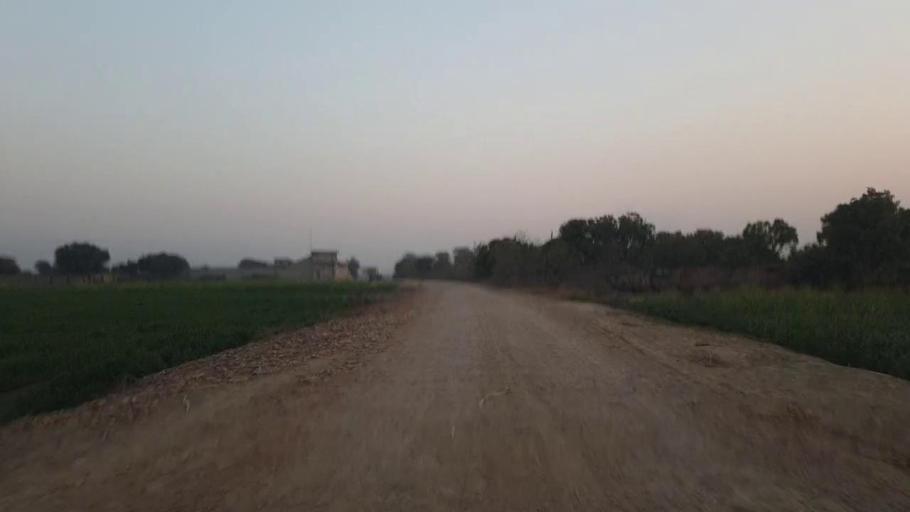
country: PK
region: Sindh
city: Tando Allahyar
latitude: 25.4451
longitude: 68.7644
